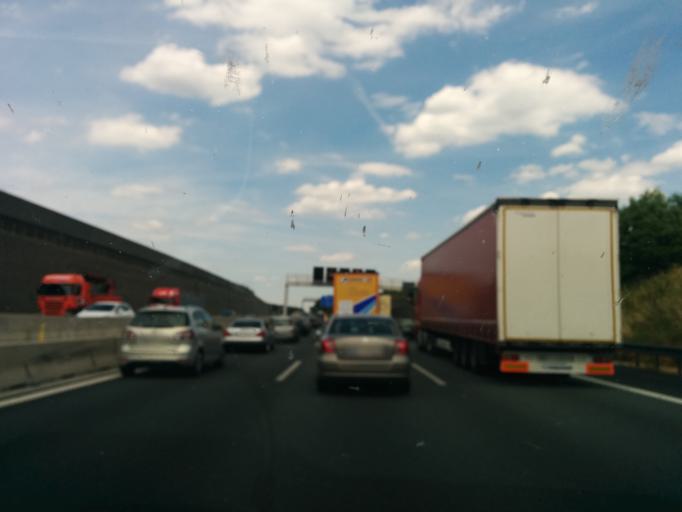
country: DE
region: Bavaria
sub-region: Regierungsbezirk Mittelfranken
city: Wendelstein
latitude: 49.3534
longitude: 11.1059
